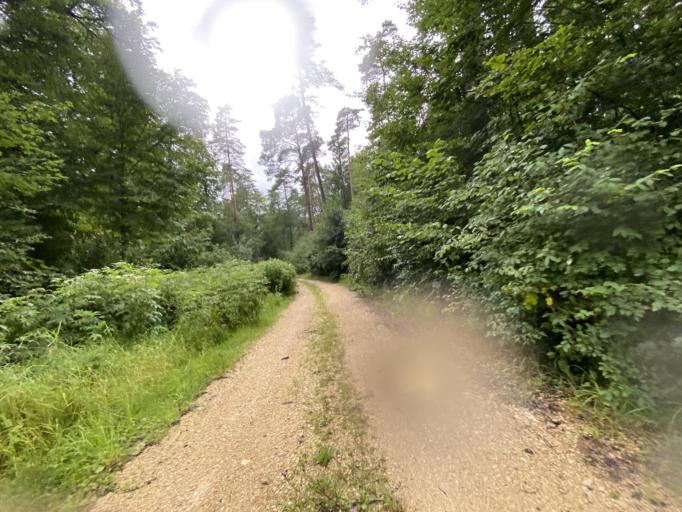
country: DE
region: Baden-Wuerttemberg
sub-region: Tuebingen Region
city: Sigmaringen
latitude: 48.1240
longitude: 9.2238
